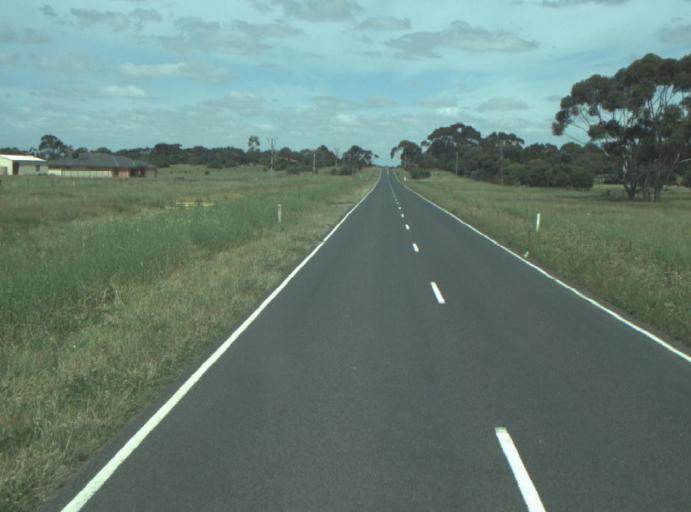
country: AU
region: Victoria
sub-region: Greater Geelong
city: Lara
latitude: -38.0181
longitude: 144.4464
